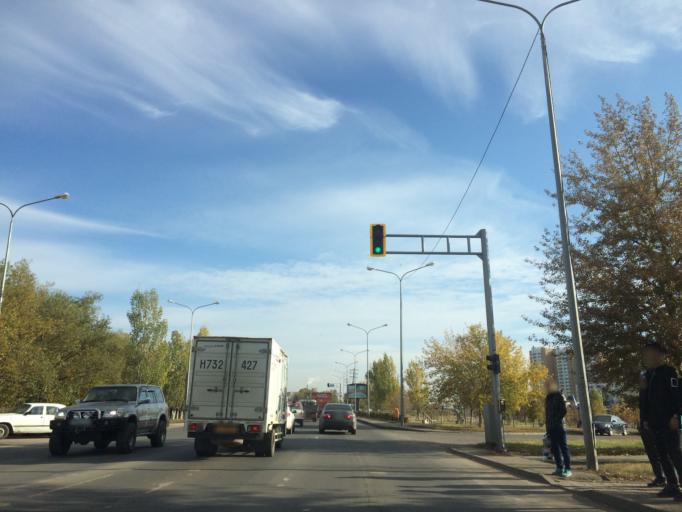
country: KZ
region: Astana Qalasy
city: Astana
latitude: 51.1596
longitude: 71.4661
